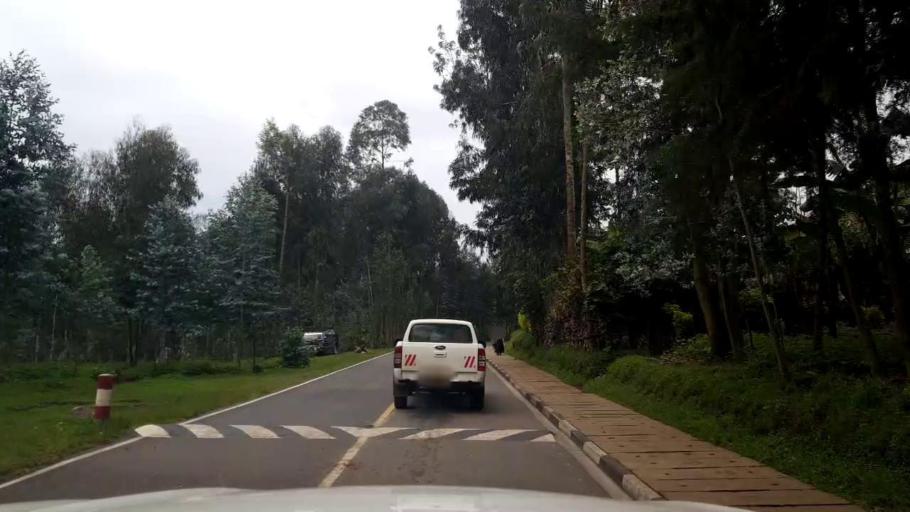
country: RW
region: Northern Province
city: Musanze
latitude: -1.4531
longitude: 29.6069
